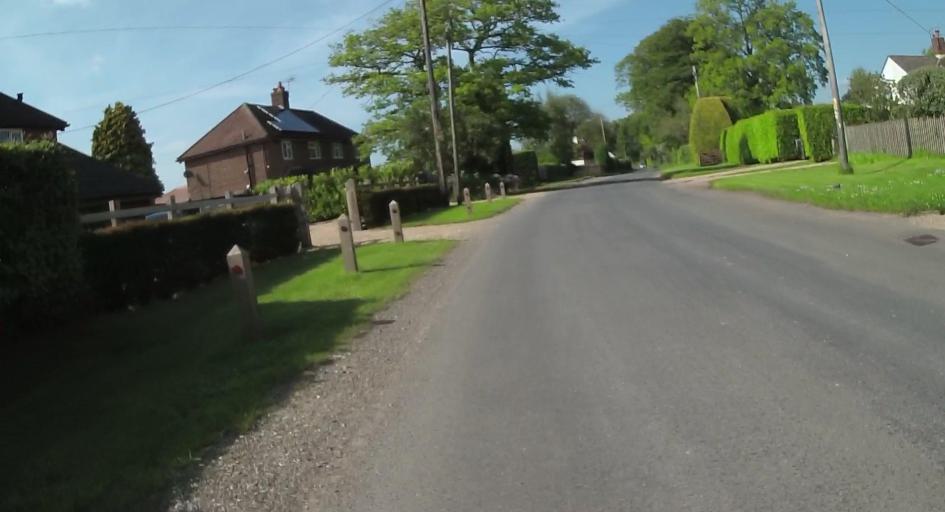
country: GB
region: England
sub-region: Hampshire
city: Four Marks
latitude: 51.1515
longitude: -1.0564
